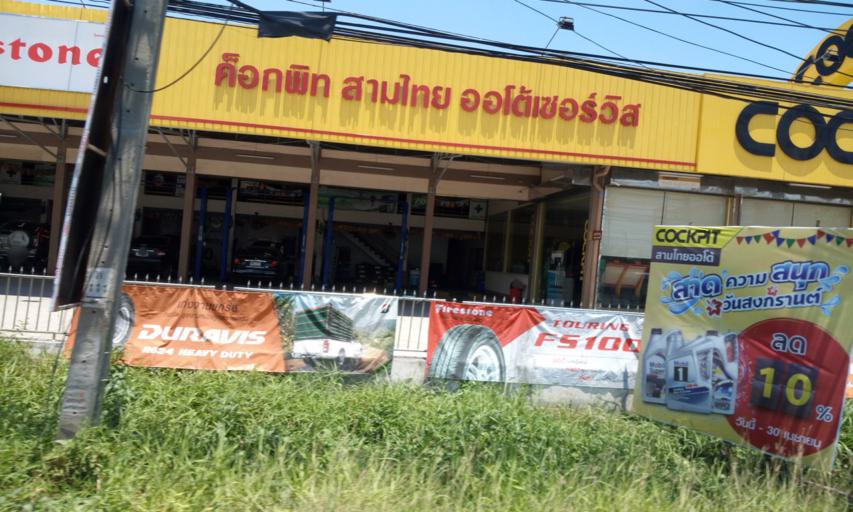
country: TH
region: Bangkok
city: Bang Na
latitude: 13.6143
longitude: 100.7028
